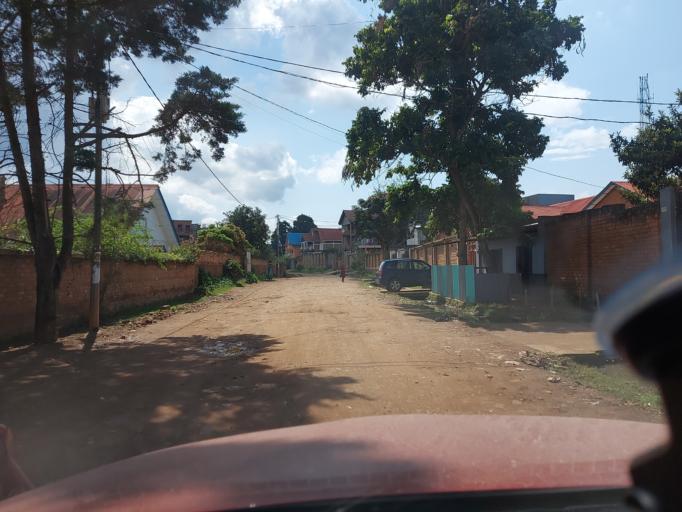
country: RW
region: Western Province
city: Cyangugu
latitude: -2.4980
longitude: 28.8861
